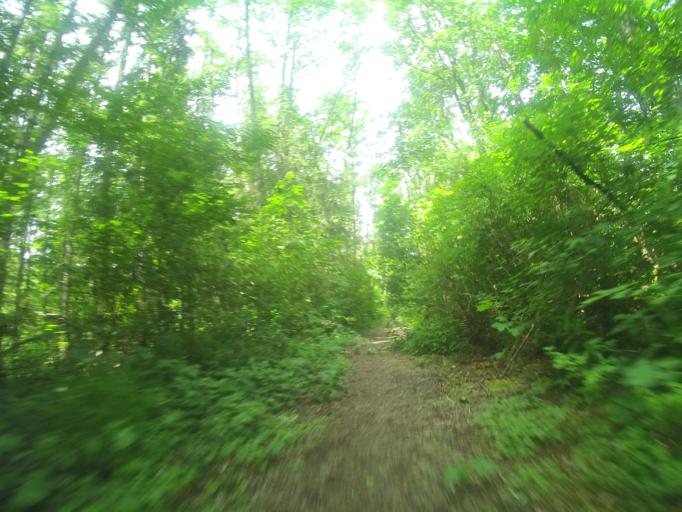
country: CA
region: British Columbia
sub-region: Fraser Valley Regional District
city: North Vancouver
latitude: 49.3216
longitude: -123.0170
